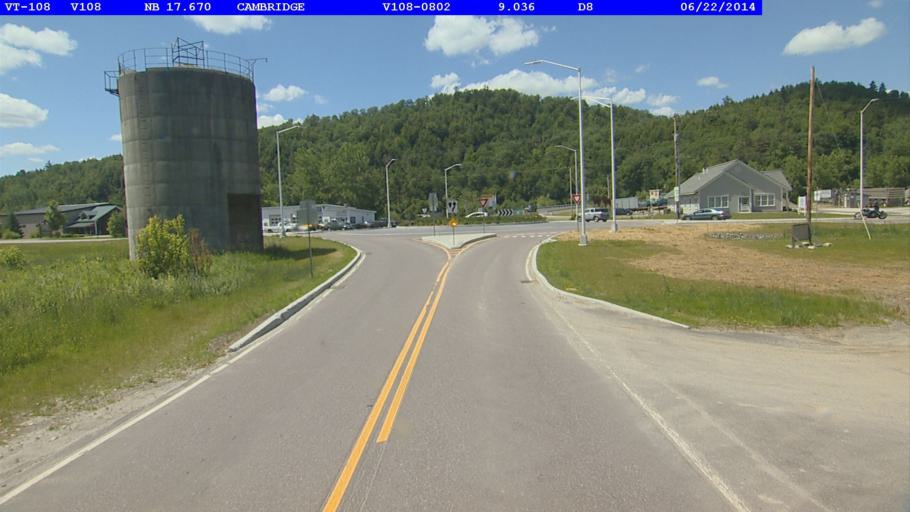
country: US
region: Vermont
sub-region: Lamoille County
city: Johnson
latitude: 44.6474
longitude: -72.8289
